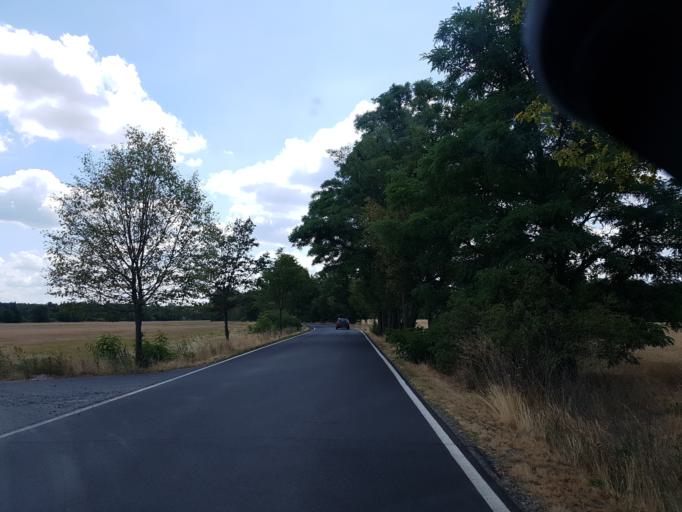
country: DE
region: Brandenburg
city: Cottbus
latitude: 51.7117
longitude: 14.4234
